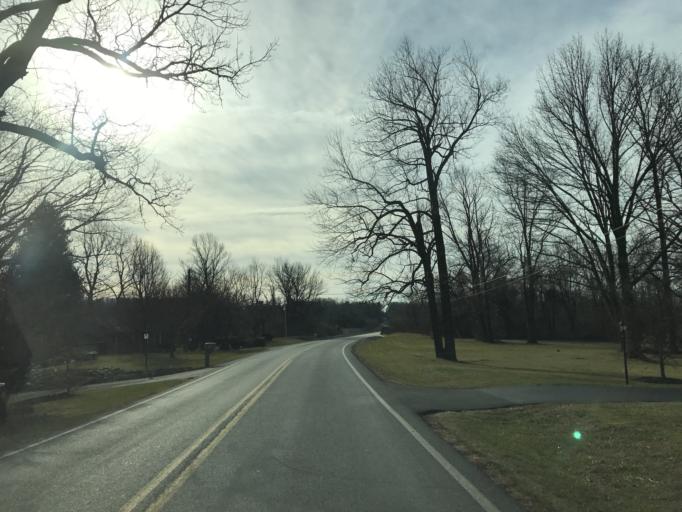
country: US
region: Maryland
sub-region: Frederick County
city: Braddock Heights
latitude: 39.4463
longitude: -77.5007
